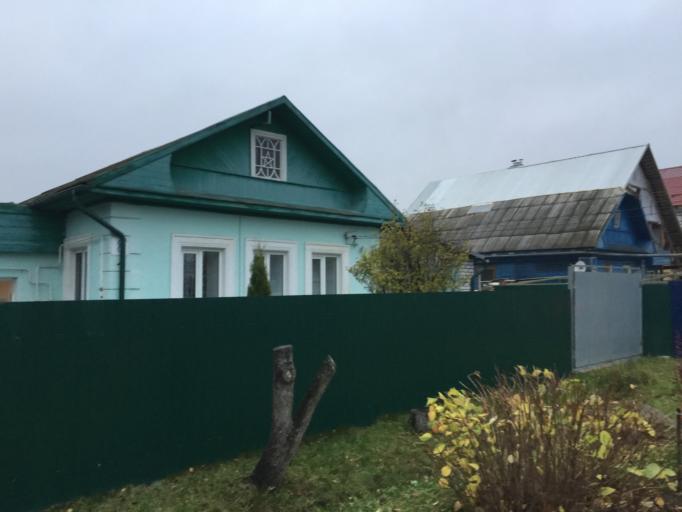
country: RU
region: Jaroslavl
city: Yaroslavl
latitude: 57.7205
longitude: 39.7730
